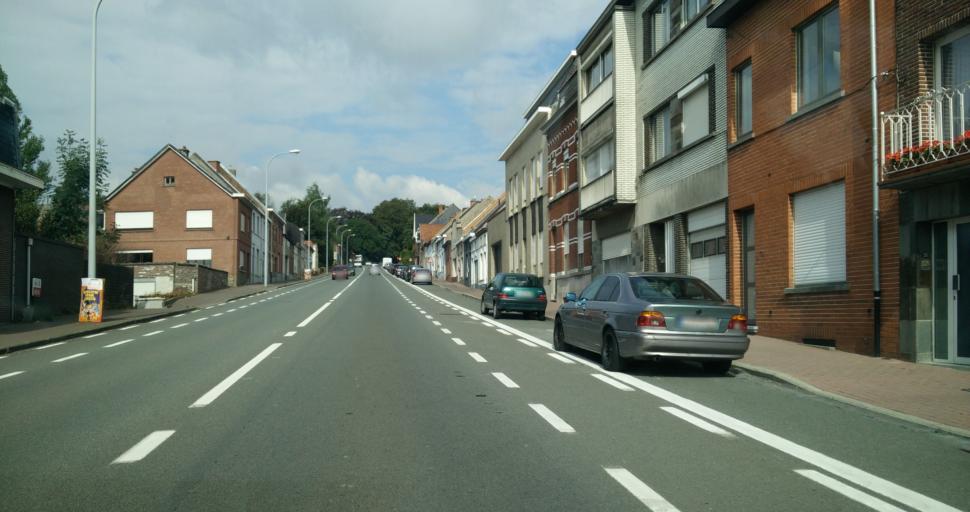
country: BE
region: Flanders
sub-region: Provincie Oost-Vlaanderen
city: Ronse
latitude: 50.7558
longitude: 3.5902
